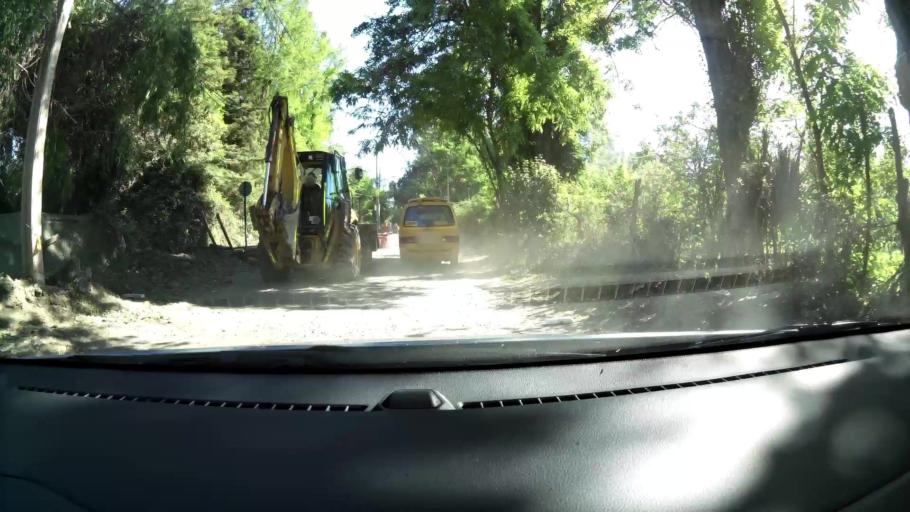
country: CL
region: Santiago Metropolitan
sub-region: Provincia de Maipo
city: San Bernardo
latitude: -33.5580
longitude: -70.7713
